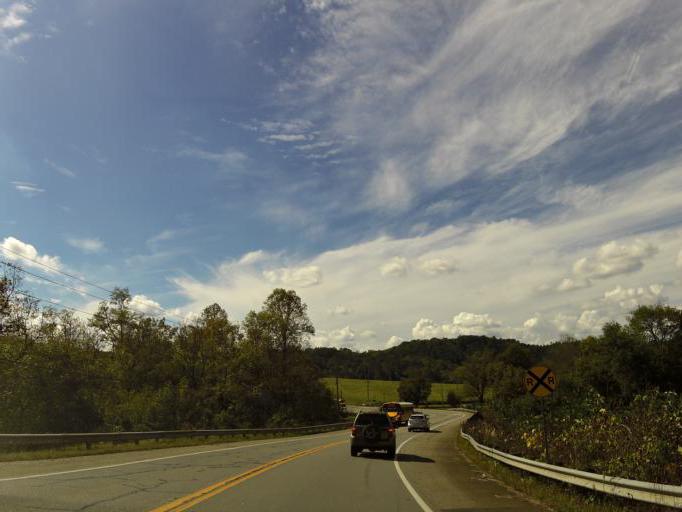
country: US
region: Georgia
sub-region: Pickens County
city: Nelson
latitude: 34.4146
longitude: -84.3658
